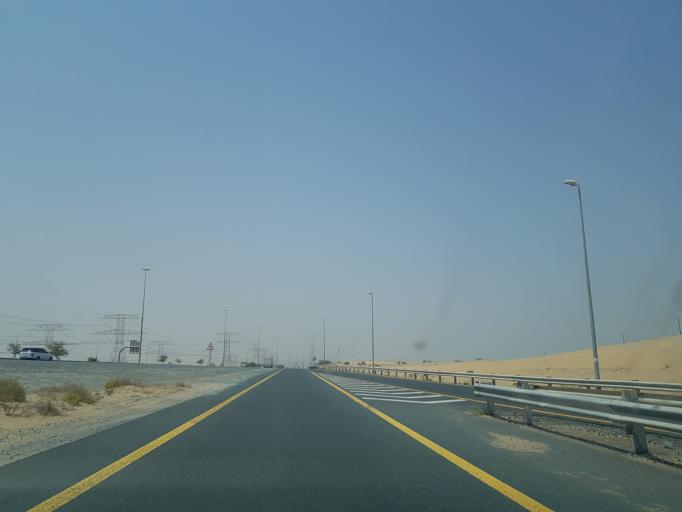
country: AE
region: Ash Shariqah
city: Sharjah
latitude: 25.1233
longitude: 55.4435
